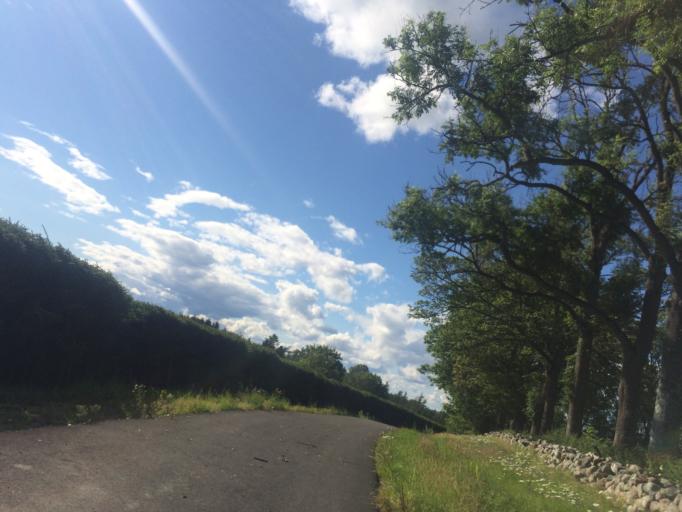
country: NO
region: Akershus
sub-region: As
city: As
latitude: 59.6712
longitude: 10.7683
